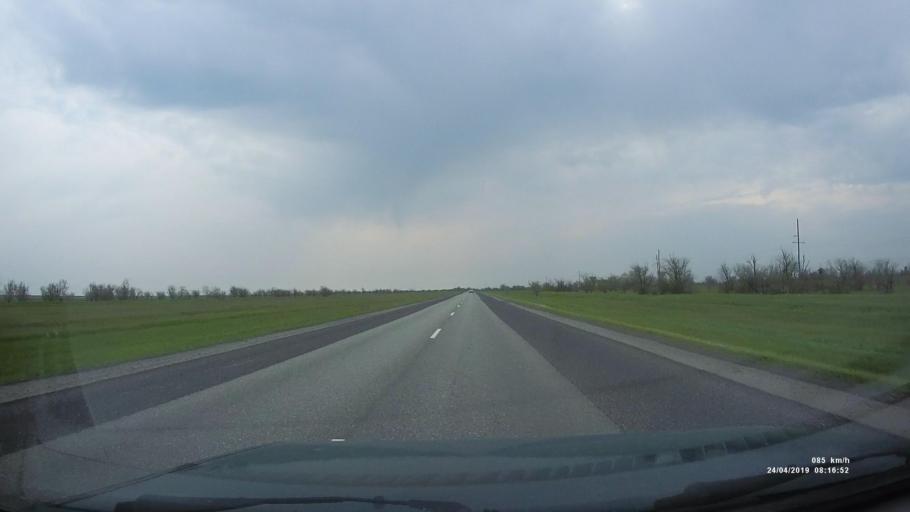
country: RU
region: Kalmykiya
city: Priyutnoye
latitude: 46.0985
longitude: 43.6199
